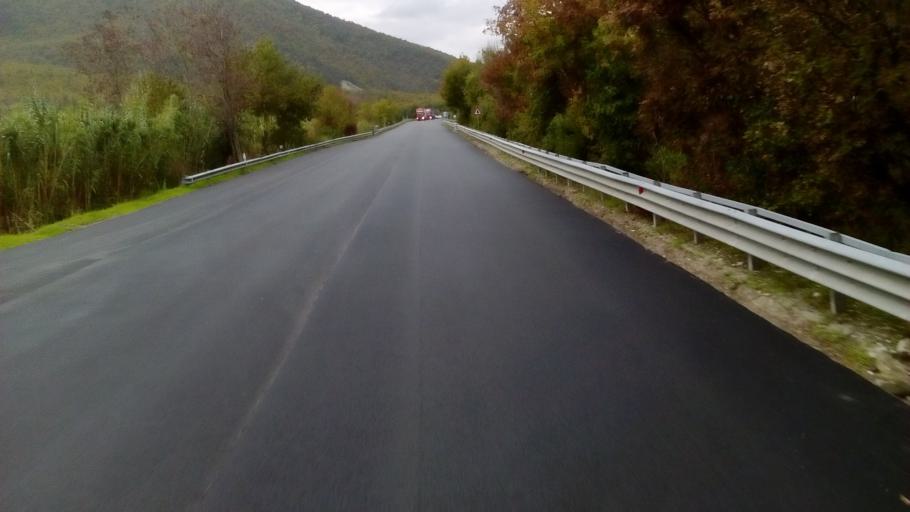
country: IT
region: Molise
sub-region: Provincia di Campobasso
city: Montemitro
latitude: 41.9081
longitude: 14.6497
